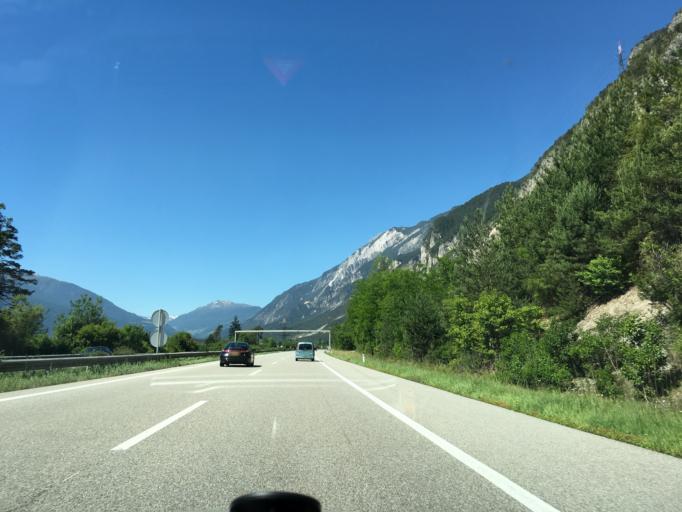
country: AT
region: Tyrol
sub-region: Politischer Bezirk Imst
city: Haiming
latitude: 47.2678
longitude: 10.9011
